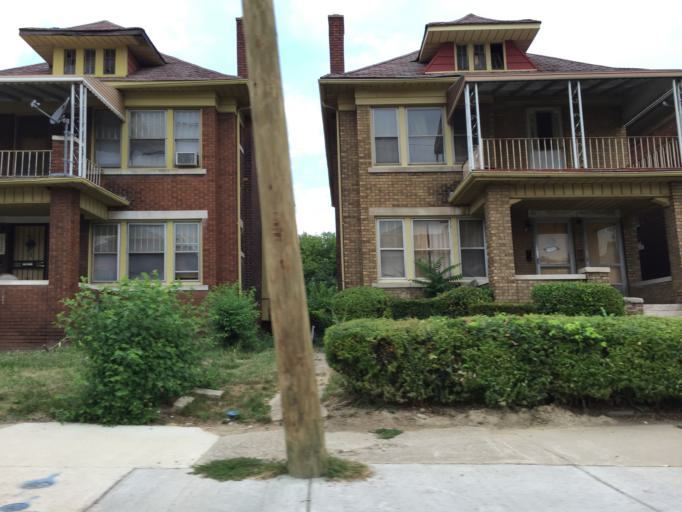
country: US
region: Michigan
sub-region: Wayne County
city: Highland Park
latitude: 42.3779
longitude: -83.0954
